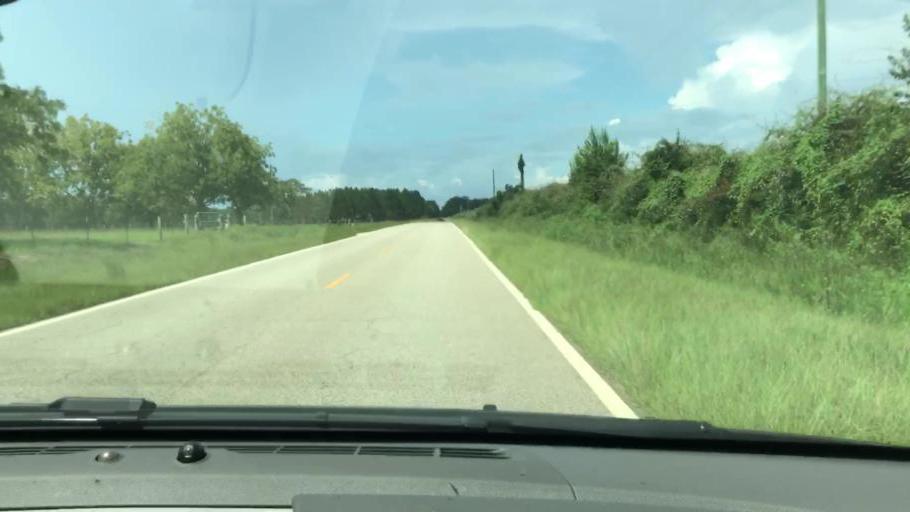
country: US
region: Georgia
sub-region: Seminole County
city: Donalsonville
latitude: 31.1397
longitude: -84.9951
